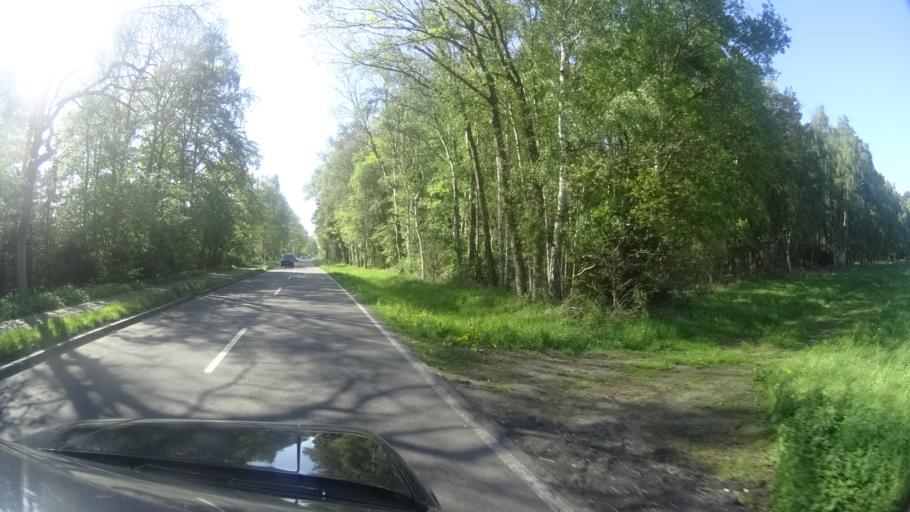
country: DE
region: Mecklenburg-Vorpommern
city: Ostseebad Dierhagen
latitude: 54.2685
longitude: 12.3481
